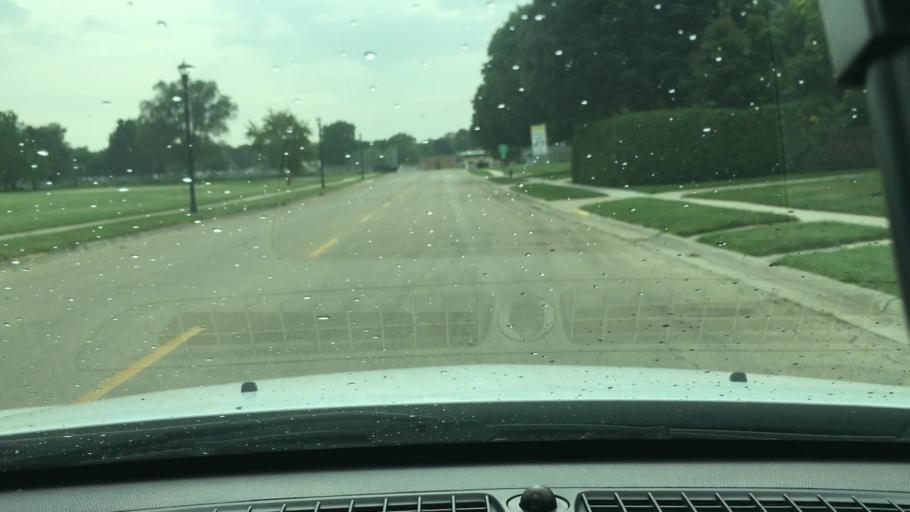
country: US
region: Illinois
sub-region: Ogle County
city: Rochelle
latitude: 41.9306
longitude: -89.0583
